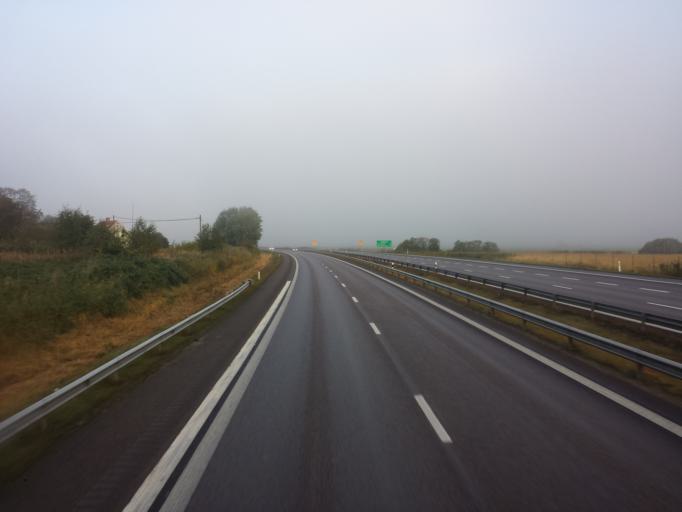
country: SE
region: Halland
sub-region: Kungsbacka Kommun
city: Fjaeras kyrkby
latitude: 57.4333
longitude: 12.1503
